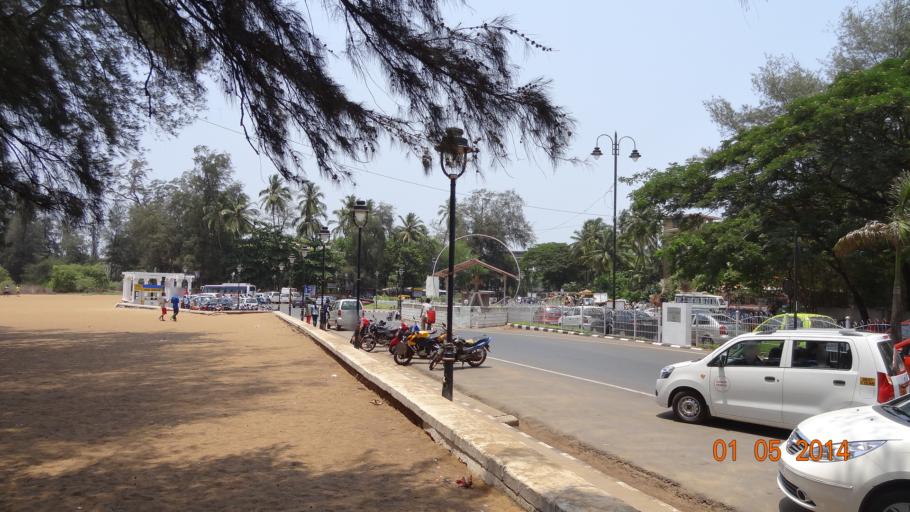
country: IN
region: Goa
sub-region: North Goa
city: Panaji
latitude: 15.4826
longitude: 73.8088
